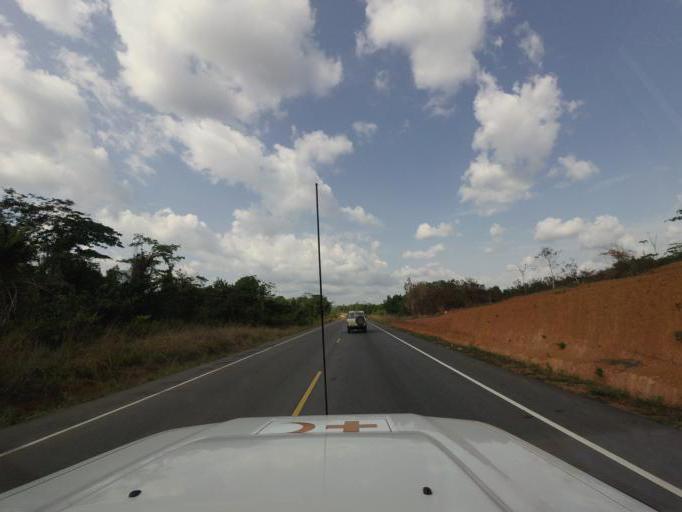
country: LR
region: Bong
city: Gbarnga
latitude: 6.9632
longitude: -9.6157
